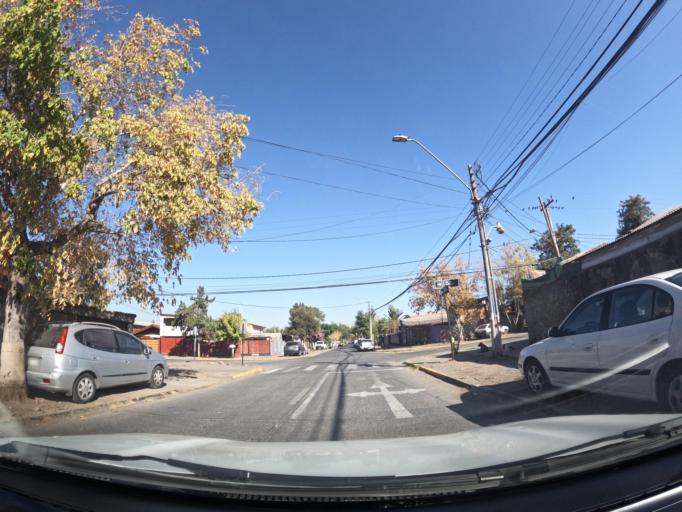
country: CL
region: Santiago Metropolitan
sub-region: Provincia de Santiago
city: Villa Presidente Frei, Nunoa, Santiago, Chile
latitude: -33.4663
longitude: -70.5689
